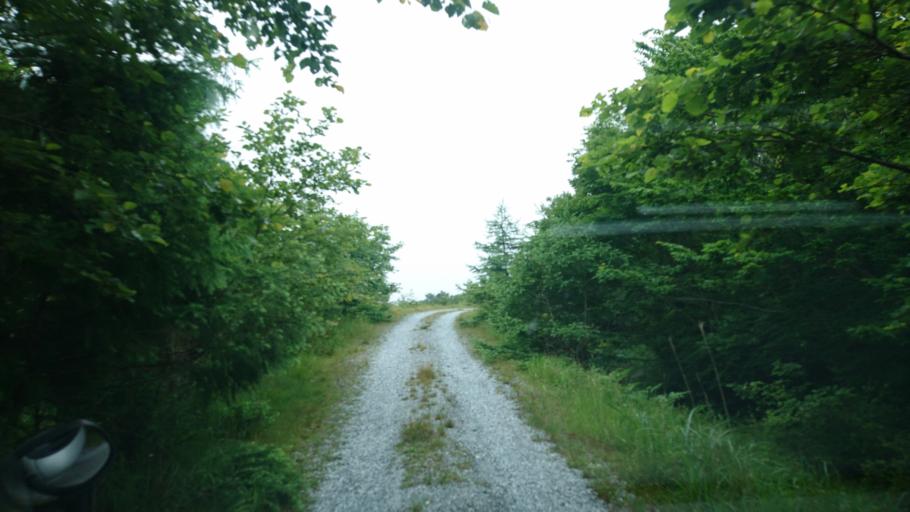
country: JP
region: Iwate
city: Kamaishi
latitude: 39.1751
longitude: 141.7921
